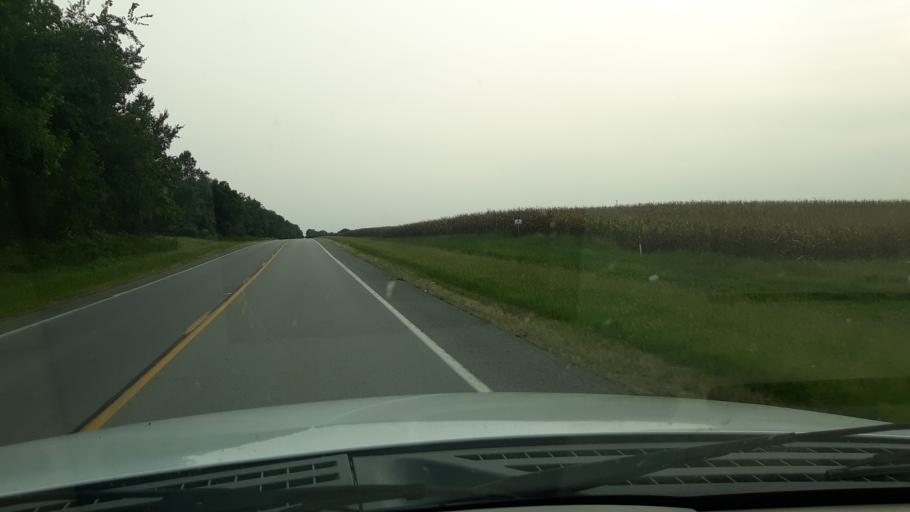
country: US
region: Illinois
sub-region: Edwards County
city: Grayville
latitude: 38.1748
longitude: -88.0524
